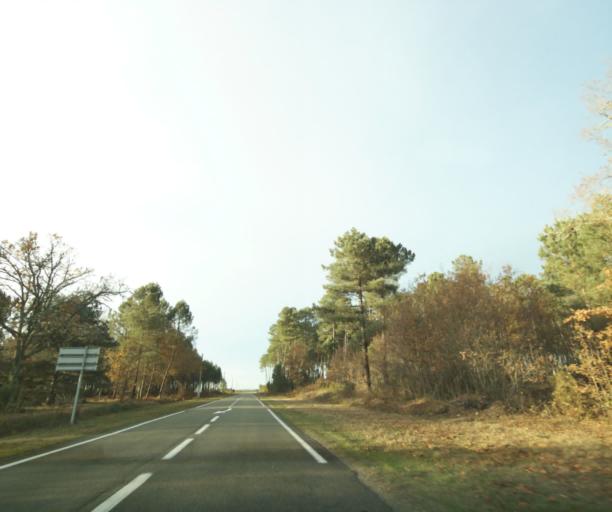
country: FR
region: Aquitaine
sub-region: Departement des Landes
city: Gabarret
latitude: 44.0691
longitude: -0.0609
